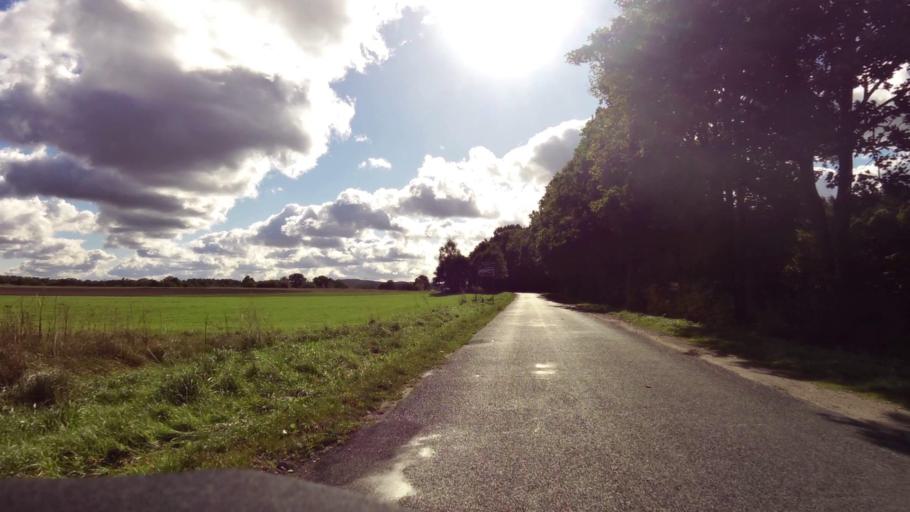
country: PL
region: West Pomeranian Voivodeship
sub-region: Powiat bialogardzki
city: Bialogard
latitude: 53.9974
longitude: 16.0624
